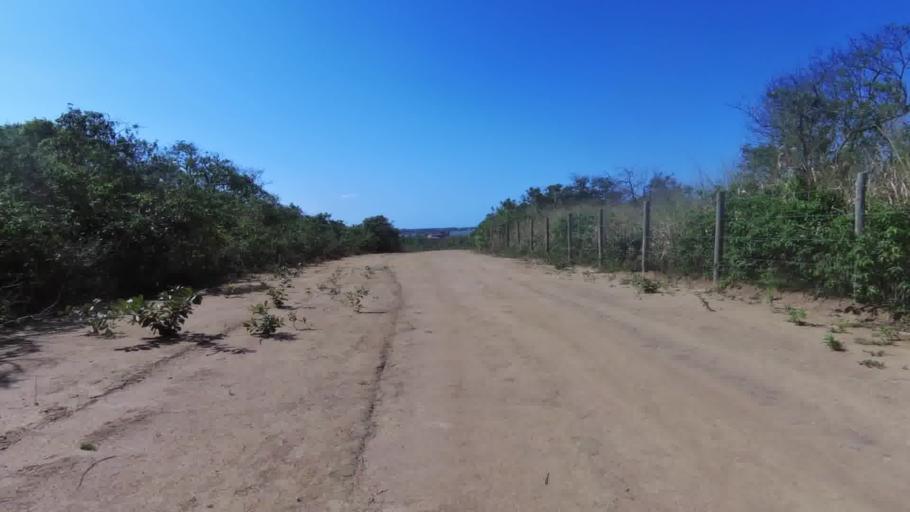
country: BR
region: Espirito Santo
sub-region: Piuma
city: Piuma
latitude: -20.8302
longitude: -40.6224
